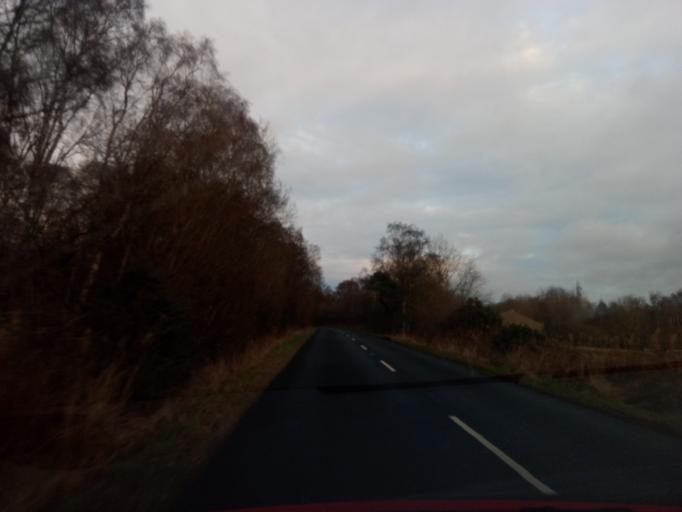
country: GB
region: England
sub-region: Northumberland
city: Morpeth
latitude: 55.1342
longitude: -1.7379
